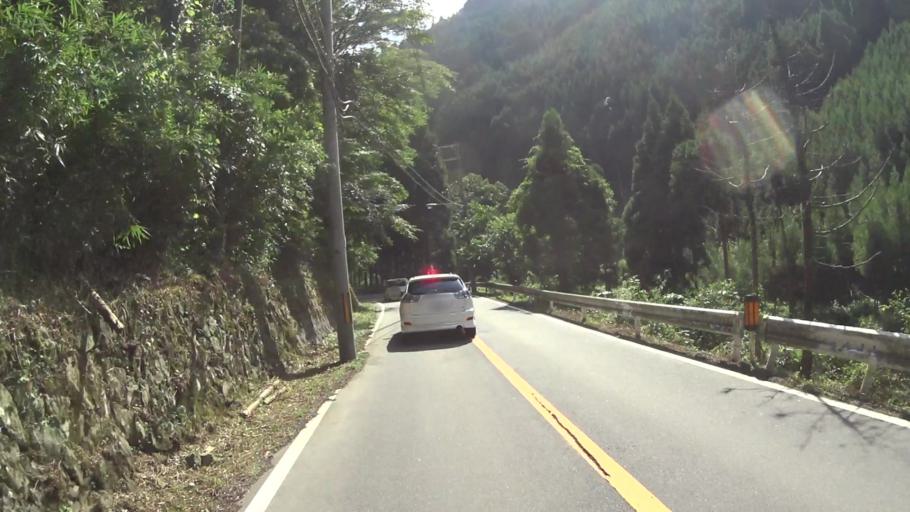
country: JP
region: Kyoto
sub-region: Kyoto-shi
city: Kamigyo-ku
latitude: 35.1027
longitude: 135.6769
